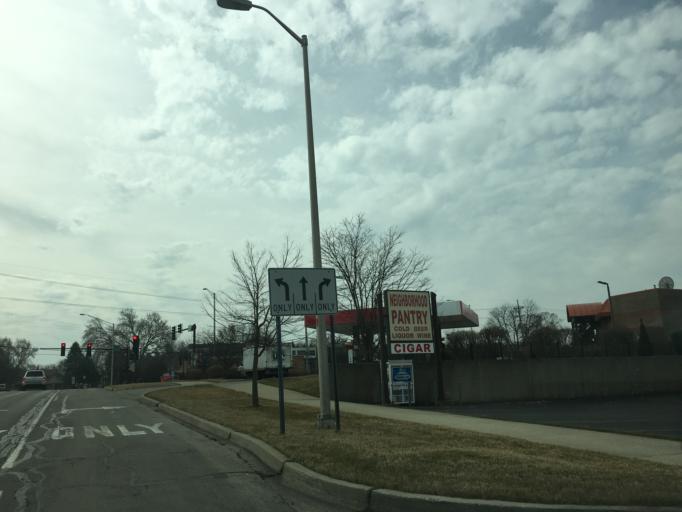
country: US
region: Illinois
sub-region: DuPage County
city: Hanover Park
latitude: 42.0047
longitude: -88.1192
